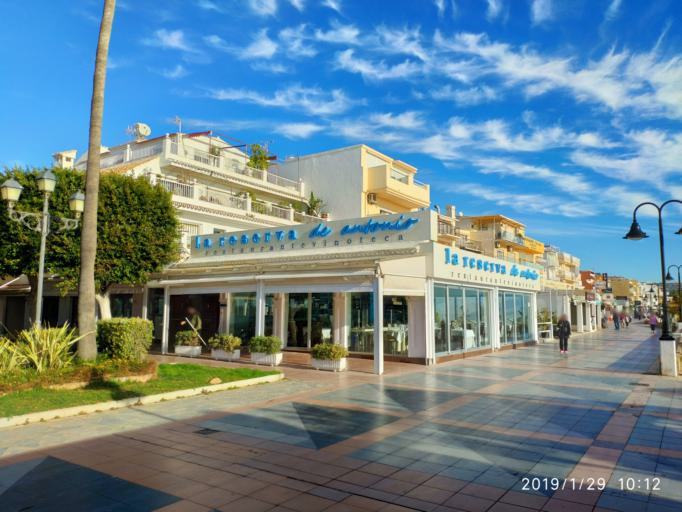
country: ES
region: Andalusia
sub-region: Provincia de Malaga
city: Torremolinos
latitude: 36.6083
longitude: -4.5047
